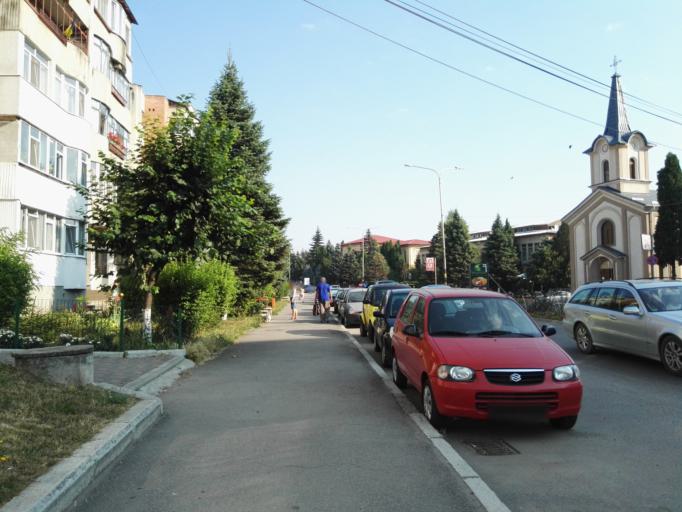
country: RO
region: Suceava
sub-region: Municipiul Falticeni
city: Falticeni
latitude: 47.4616
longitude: 26.3024
